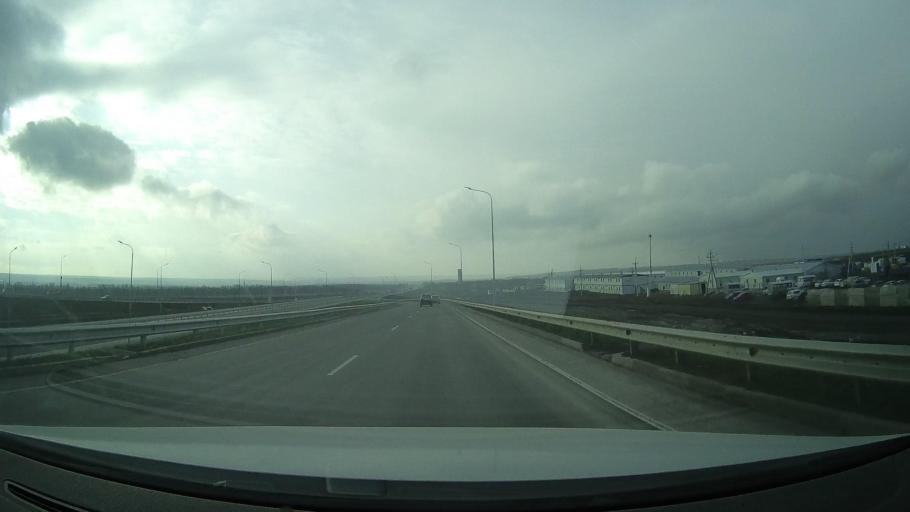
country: RU
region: Rostov
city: Grushevskaya
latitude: 47.4831
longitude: 39.9280
